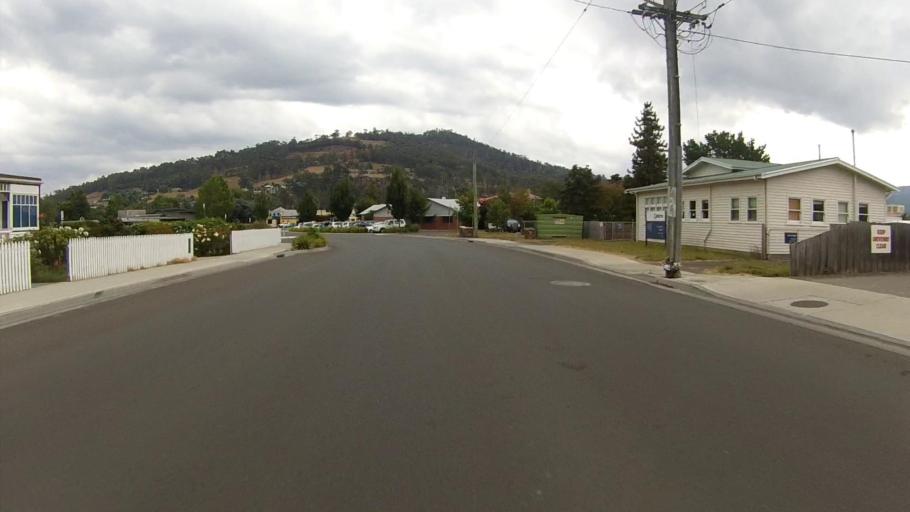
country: AU
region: Tasmania
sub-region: Huon Valley
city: Huonville
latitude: -43.0303
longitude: 147.0513
